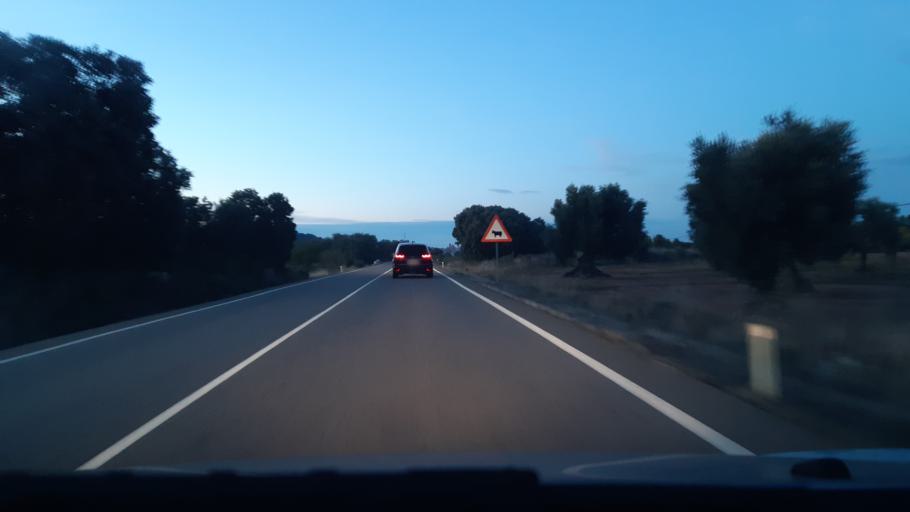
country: ES
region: Aragon
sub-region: Provincia de Teruel
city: Calaceite
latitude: 40.9961
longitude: 0.1965
